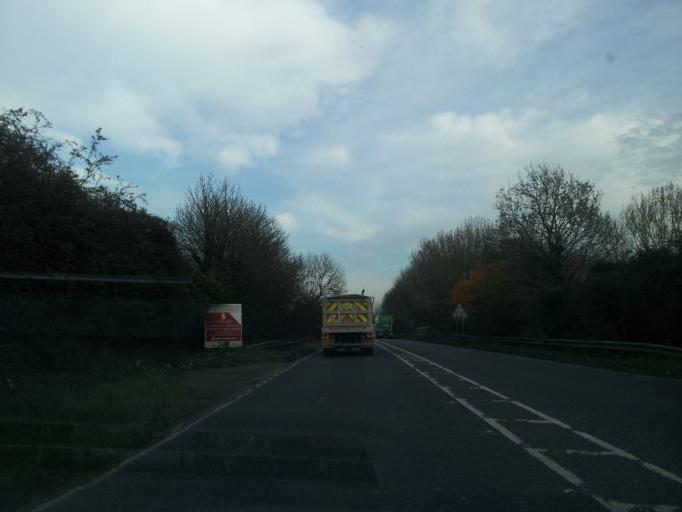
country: GB
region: England
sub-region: Cambridgeshire
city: Duxford
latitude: 52.1027
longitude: 0.1643
